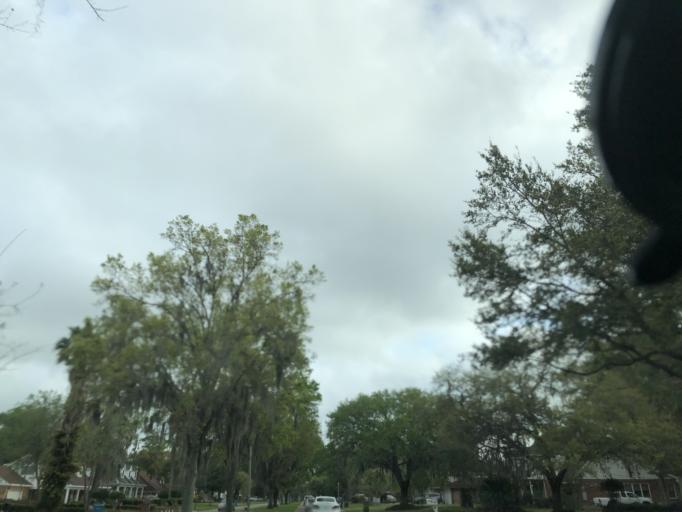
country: US
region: Louisiana
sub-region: Saint Charles Parish
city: New Sarpy
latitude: 29.9730
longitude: -90.3658
